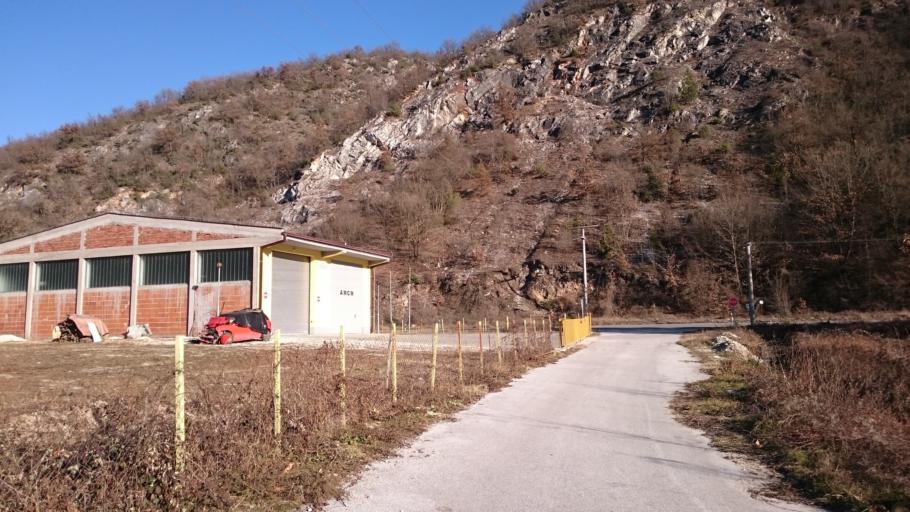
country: MK
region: Makedonski Brod
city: Makedonski Brod
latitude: 41.5115
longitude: 21.2285
